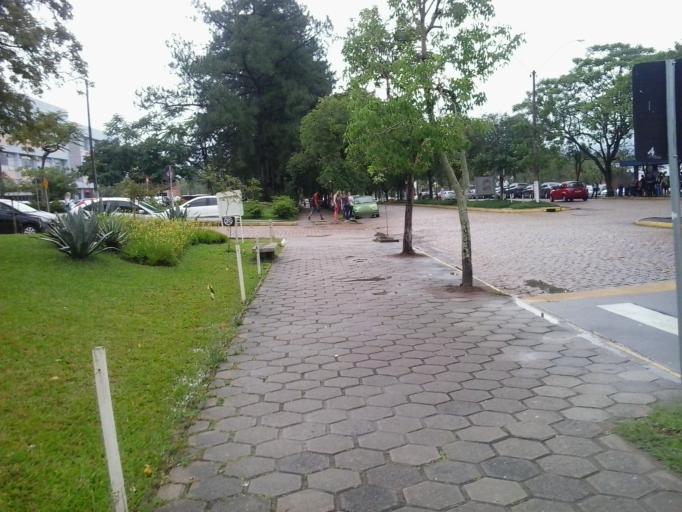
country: BR
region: Rio Grande do Sul
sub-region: Santa Maria
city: Santa Maria
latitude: -29.7141
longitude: -53.7161
